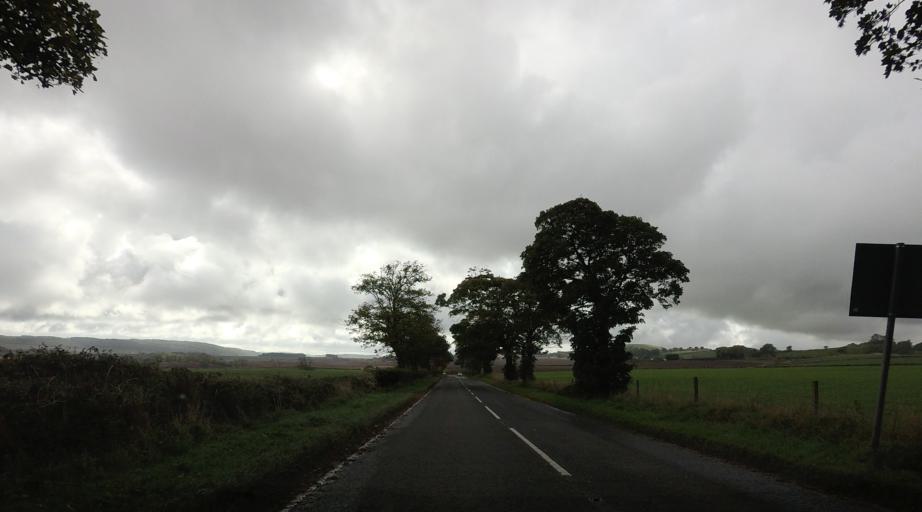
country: GB
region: Scotland
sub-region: Fife
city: Balmullo
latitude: 56.3729
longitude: -2.9298
